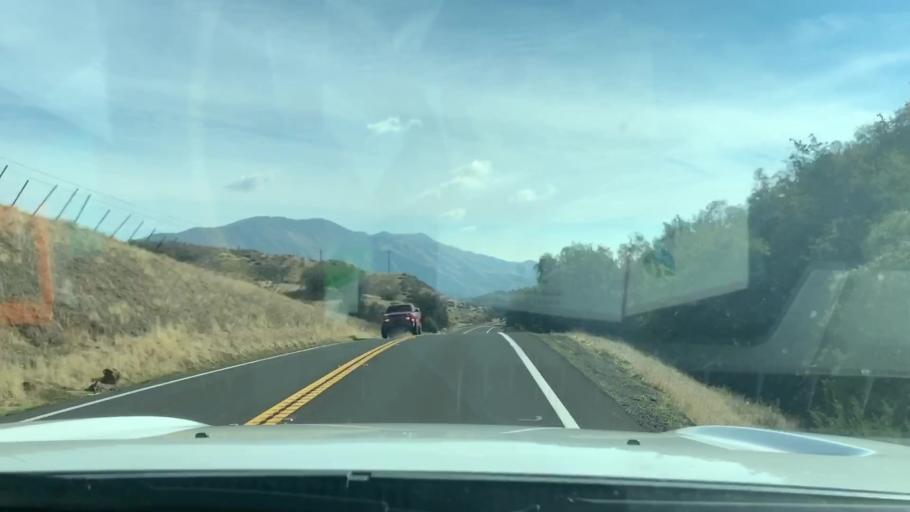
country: US
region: California
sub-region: Fresno County
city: Coalinga
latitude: 36.0908
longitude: -120.5034
